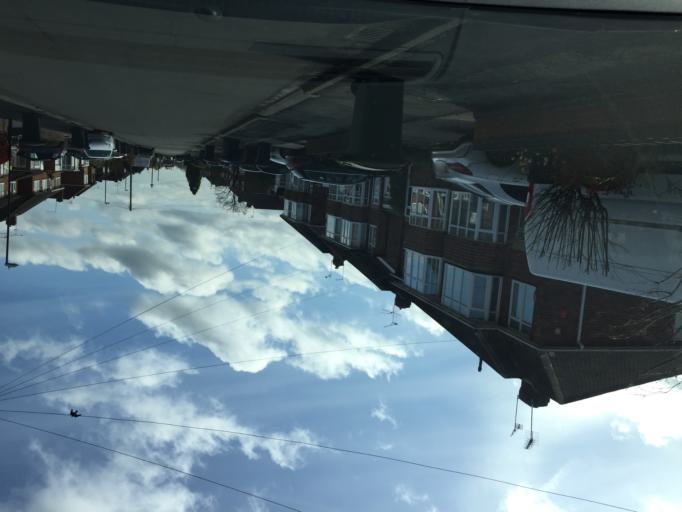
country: GB
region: England
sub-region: Coventry
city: Coventry
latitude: 52.3840
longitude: -1.5144
